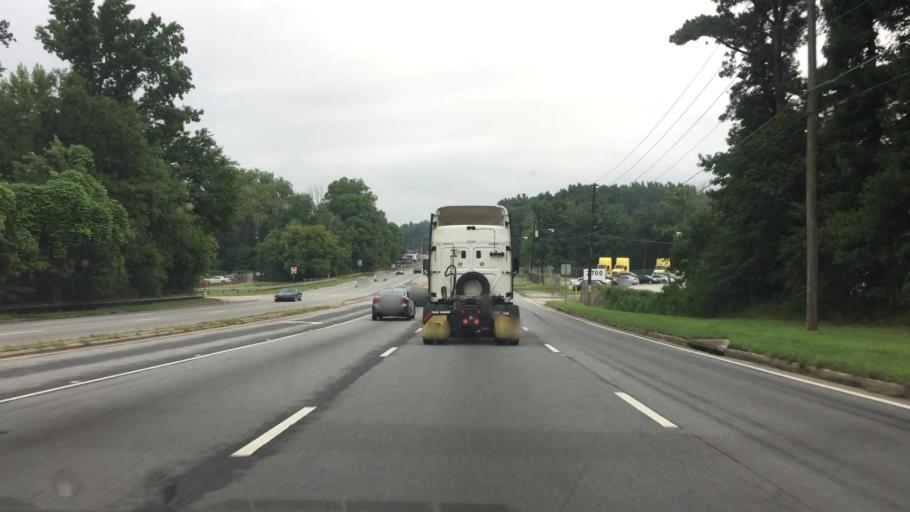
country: US
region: Georgia
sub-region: Clayton County
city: Conley
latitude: 33.6784
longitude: -84.3449
